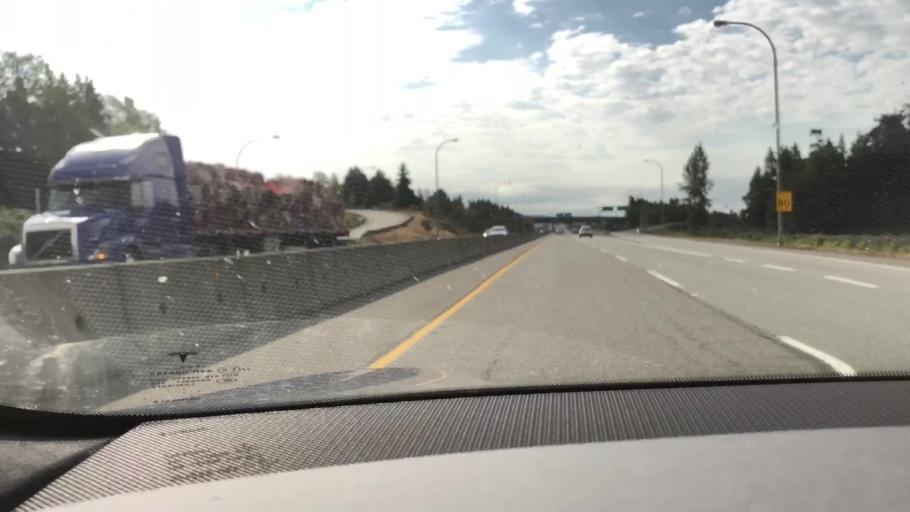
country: CA
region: British Columbia
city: Delta
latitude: 49.1062
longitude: -122.9027
